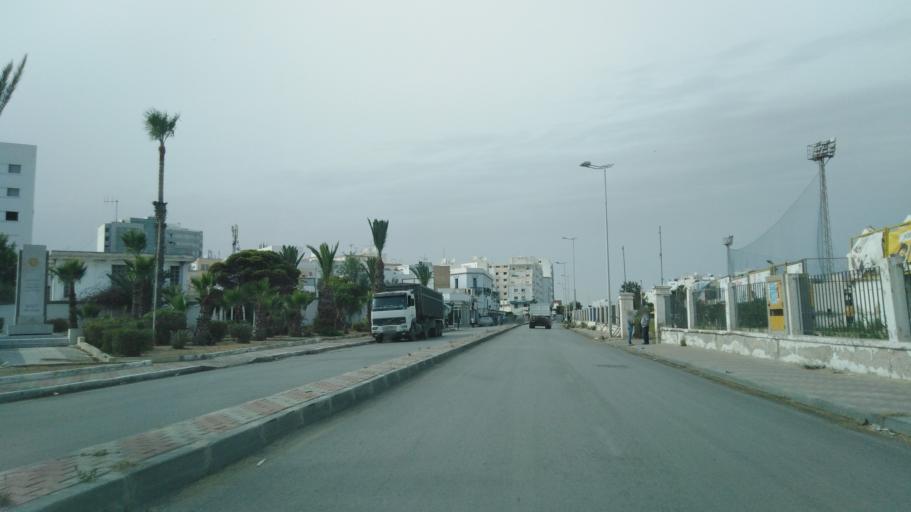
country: TN
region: Safaqis
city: Sfax
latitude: 34.7403
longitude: 10.7637
